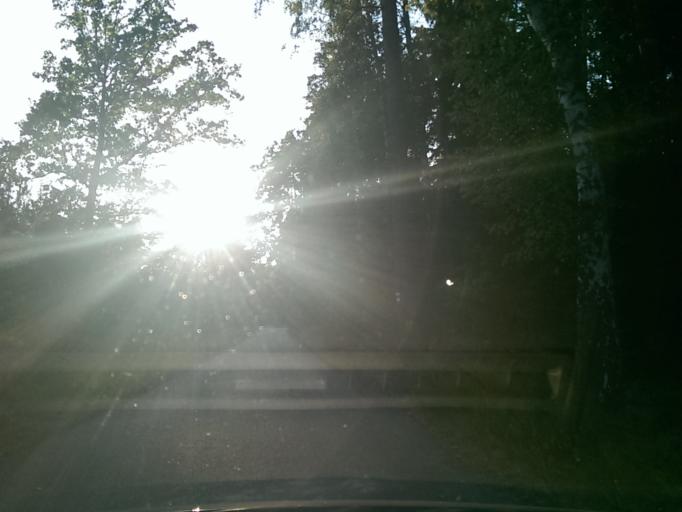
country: CZ
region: Central Bohemia
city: Bela pod Bezdezem
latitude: 50.4993
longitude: 14.7161
